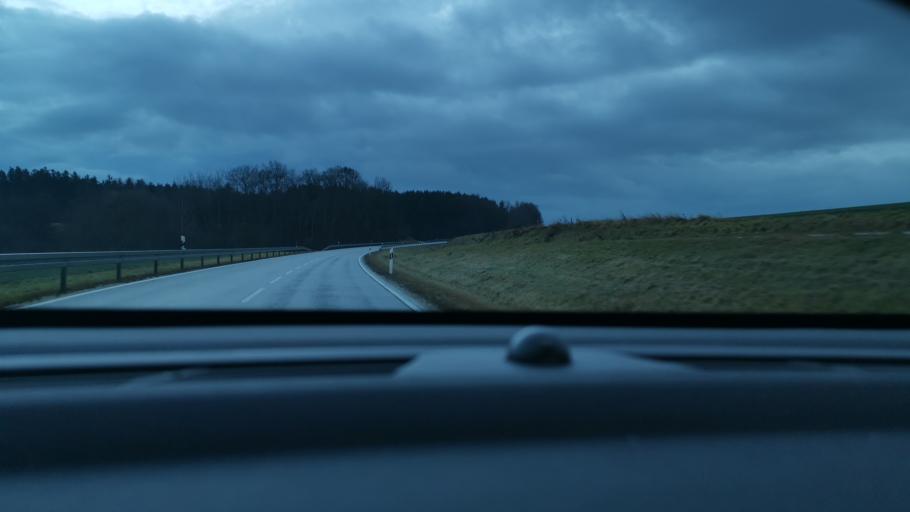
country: DE
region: Bavaria
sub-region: Swabia
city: Petersdorf
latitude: 48.5322
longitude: 11.0256
